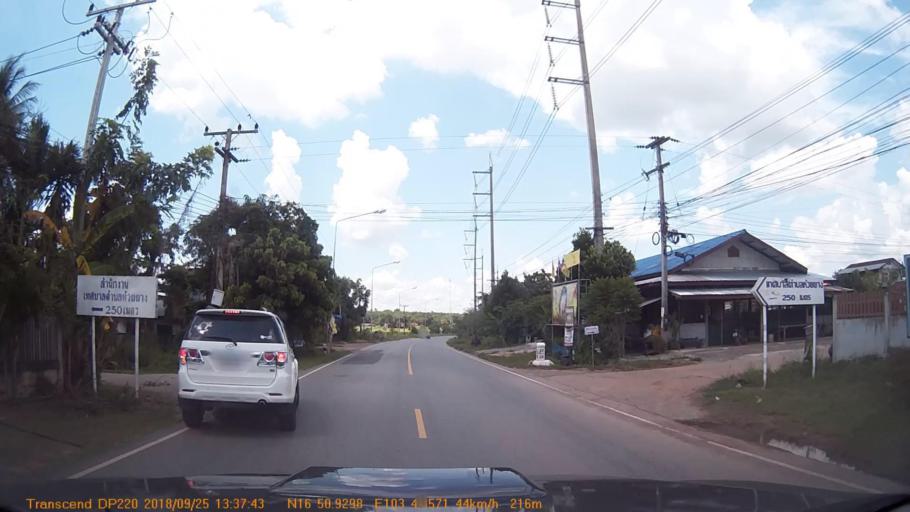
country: TH
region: Khon Kaen
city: Kranuan
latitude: 16.8489
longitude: 103.0810
